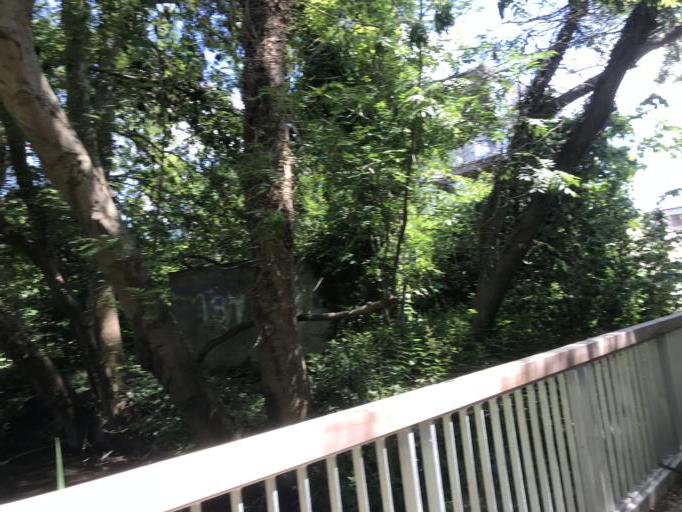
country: GB
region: England
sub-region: Cambridgeshire
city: Cambridge
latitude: 52.1881
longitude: 0.1271
